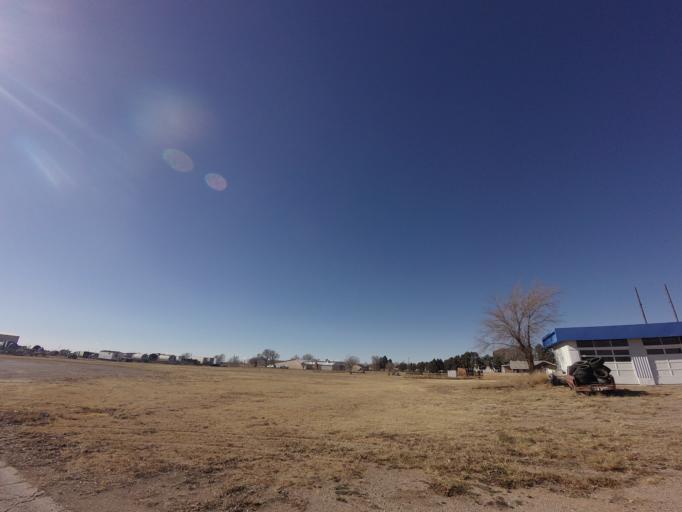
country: US
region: New Mexico
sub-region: Curry County
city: Clovis
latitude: 34.4042
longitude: -103.2366
